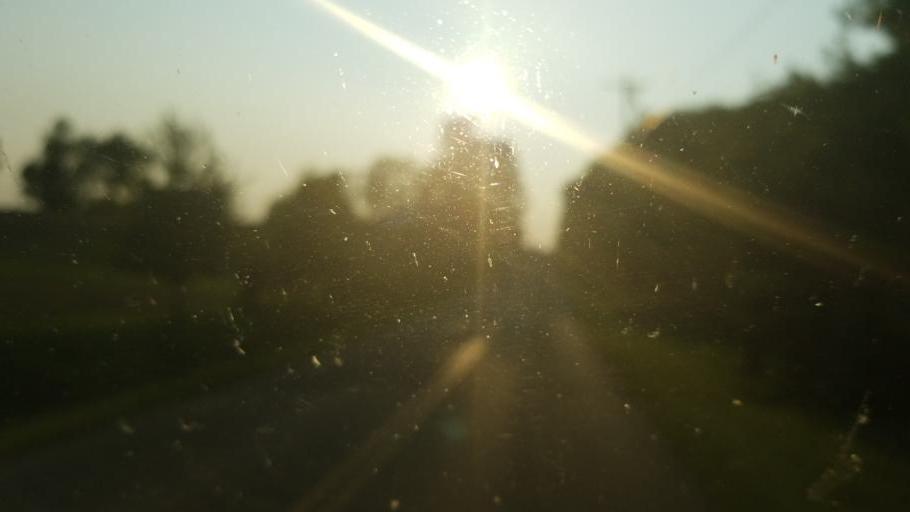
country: US
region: Ohio
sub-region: Wayne County
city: Shreve
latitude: 40.6680
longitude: -82.0009
